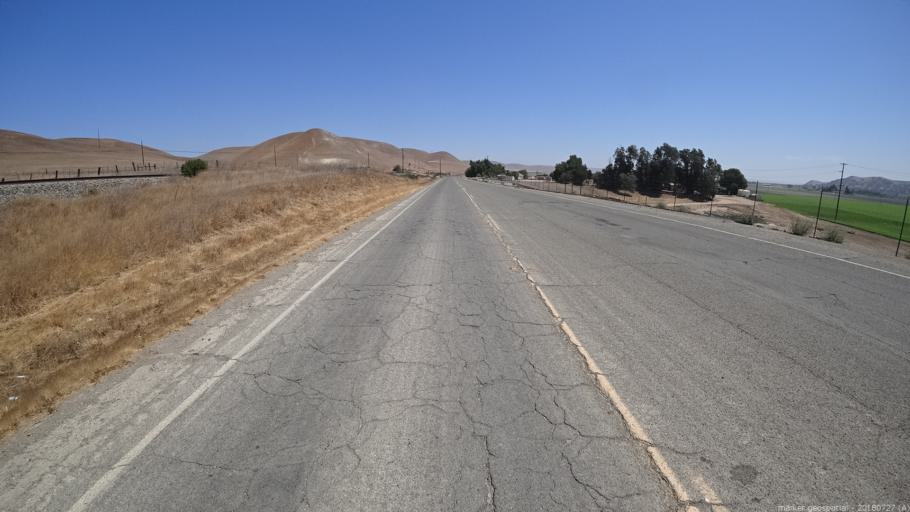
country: US
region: California
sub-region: Monterey County
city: King City
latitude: 36.1046
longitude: -120.9846
